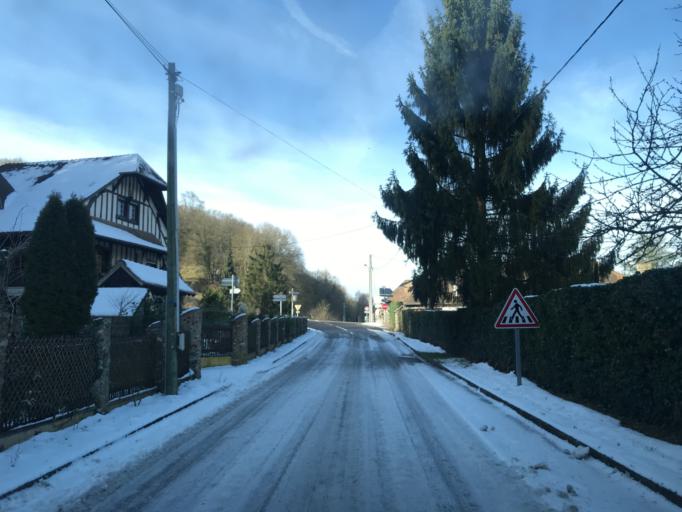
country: FR
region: Haute-Normandie
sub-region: Departement de l'Eure
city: Saint-Aubin-sur-Gaillon
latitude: 49.0872
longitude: 1.2678
